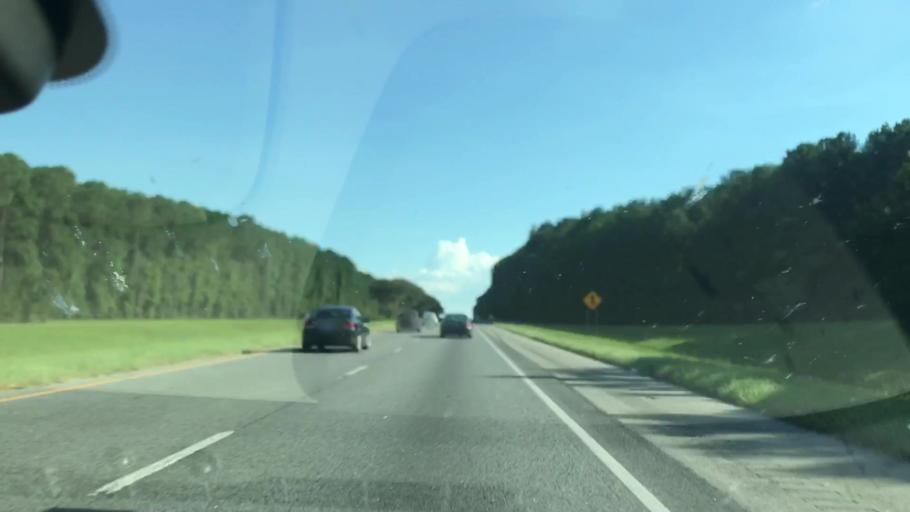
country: US
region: Georgia
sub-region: Harris County
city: Hamilton
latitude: 32.8125
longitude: -85.0214
